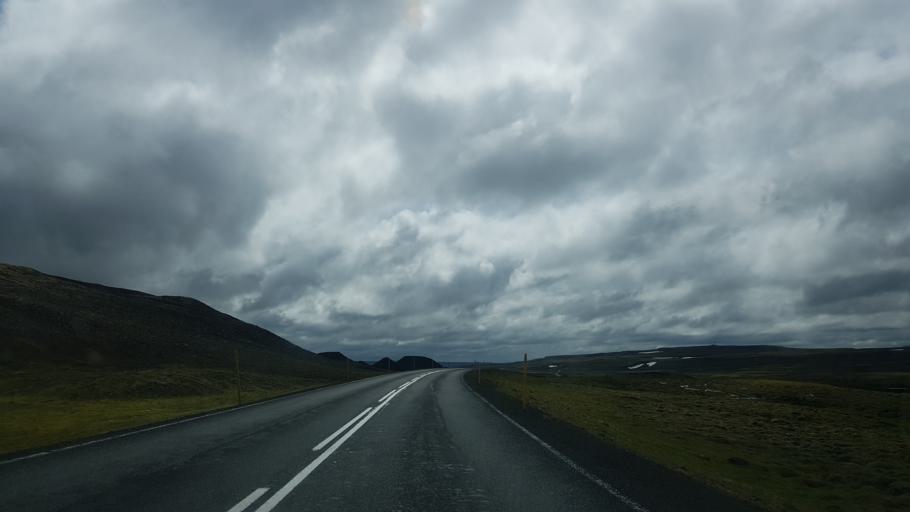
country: IS
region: West
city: Borgarnes
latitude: 64.9853
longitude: -21.0552
